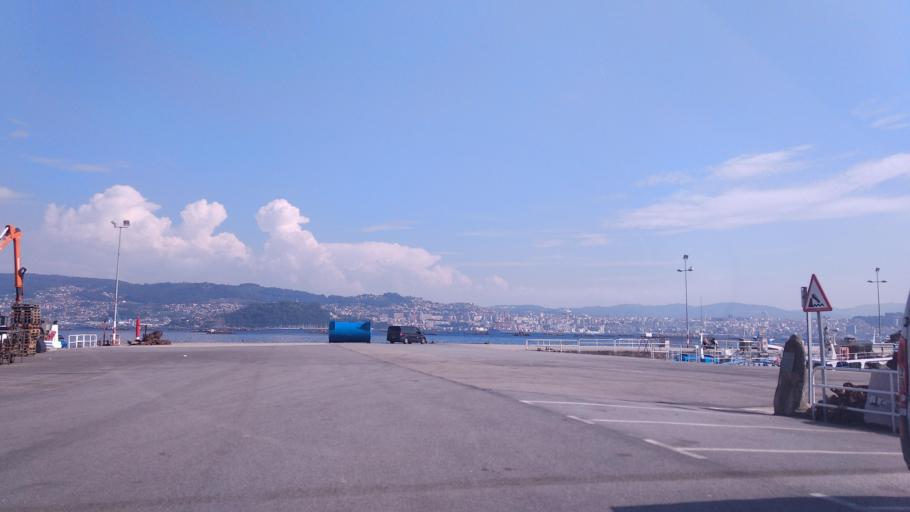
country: ES
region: Galicia
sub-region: Provincia de Pontevedra
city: Moana
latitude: 42.2737
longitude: -8.7365
